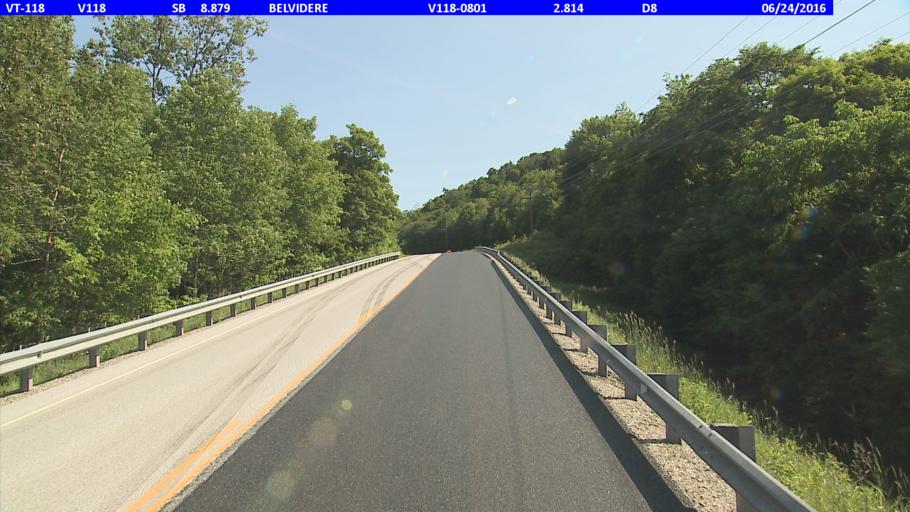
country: US
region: Vermont
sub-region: Lamoille County
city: Johnson
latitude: 44.7993
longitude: -72.6250
